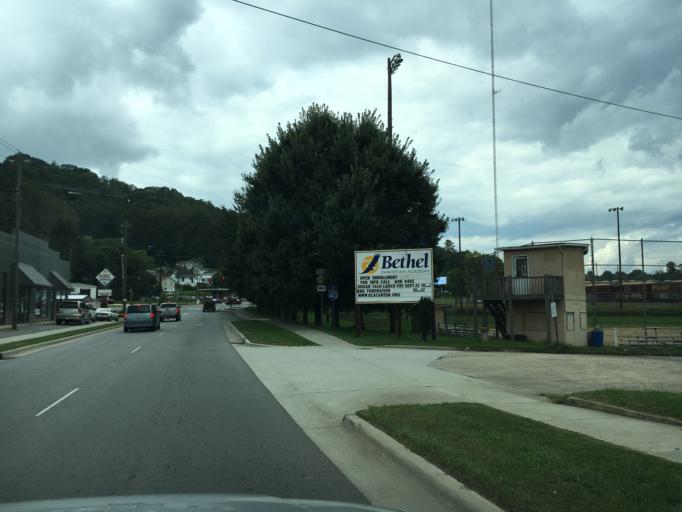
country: US
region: North Carolina
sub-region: Haywood County
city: Canton
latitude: 35.5313
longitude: -82.8435
